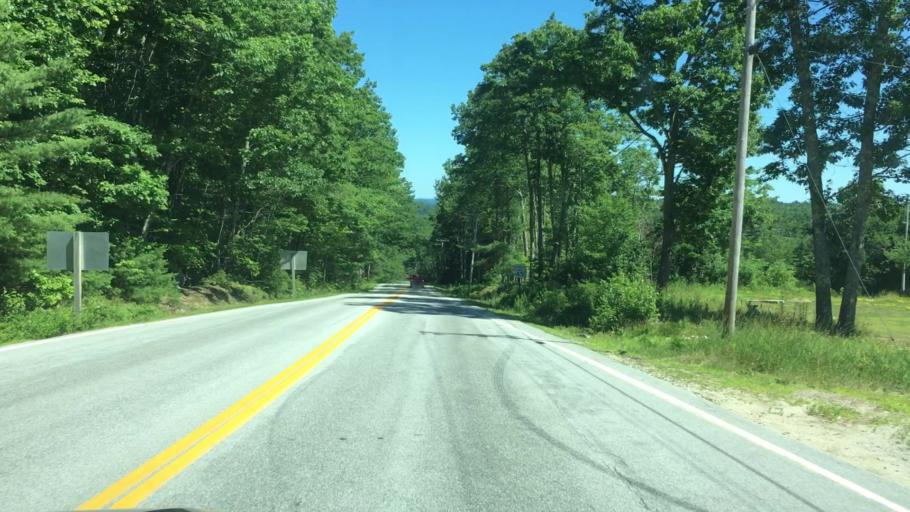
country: US
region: Maine
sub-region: Hancock County
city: Sedgwick
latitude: 44.3431
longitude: -68.6737
